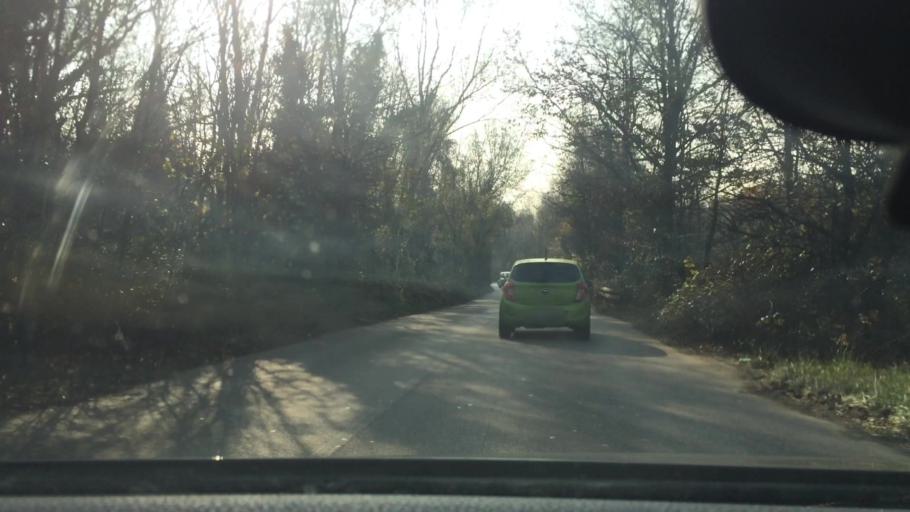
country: IT
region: Lombardy
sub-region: Citta metropolitana di Milano
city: Cesate
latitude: 45.5880
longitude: 9.0909
